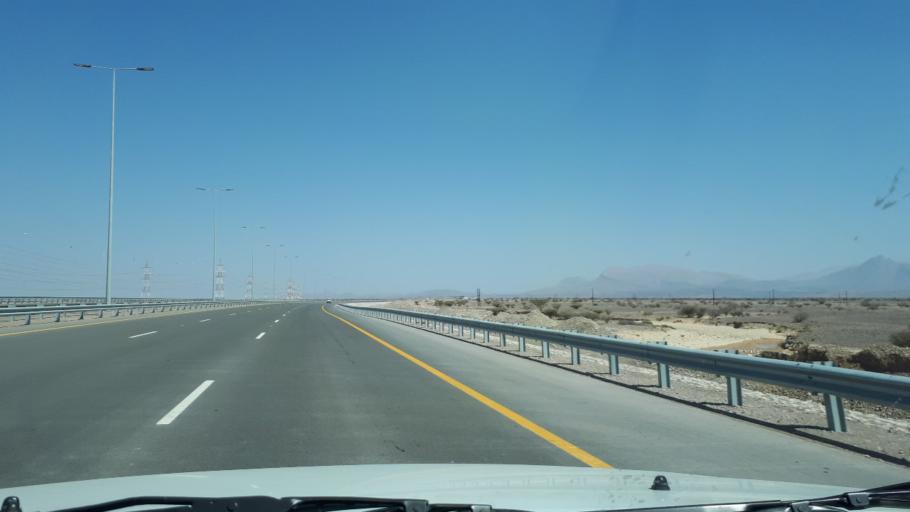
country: OM
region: Ash Sharqiyah
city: Badiyah
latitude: 22.3409
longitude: 59.1228
